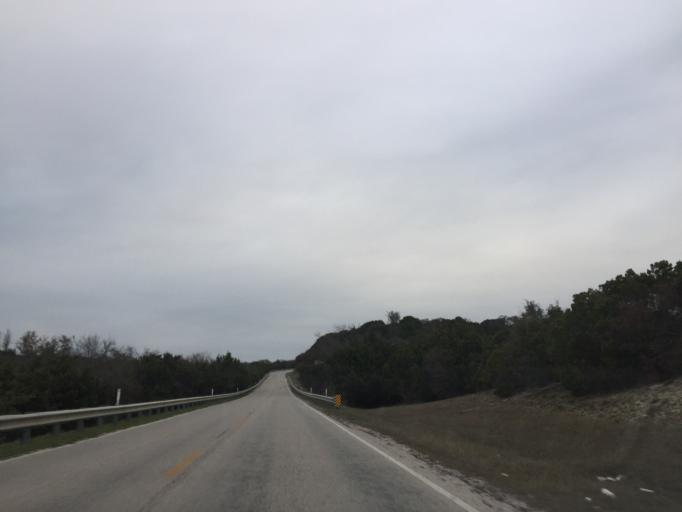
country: US
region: Texas
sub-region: Coryell County
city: Ames
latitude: 31.5013
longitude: -97.7277
